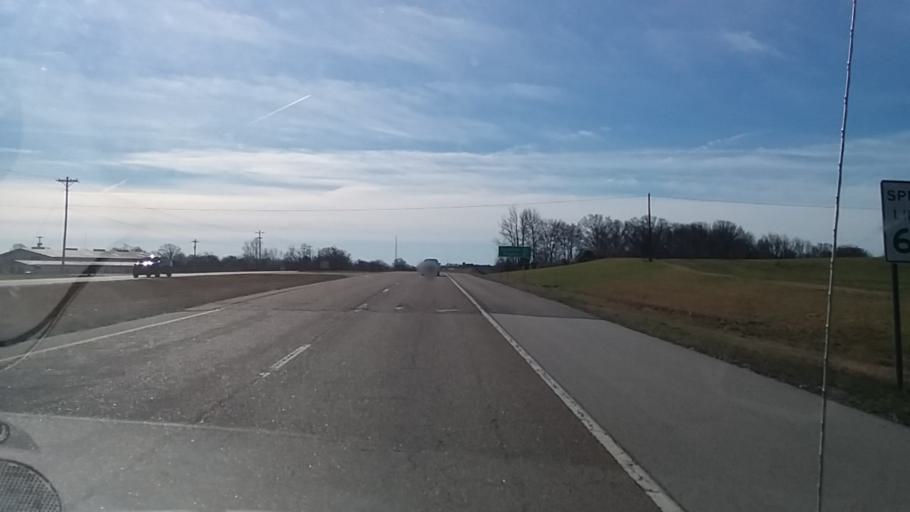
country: US
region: Tennessee
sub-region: Crockett County
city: Alamo
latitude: 35.8175
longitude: -89.1657
